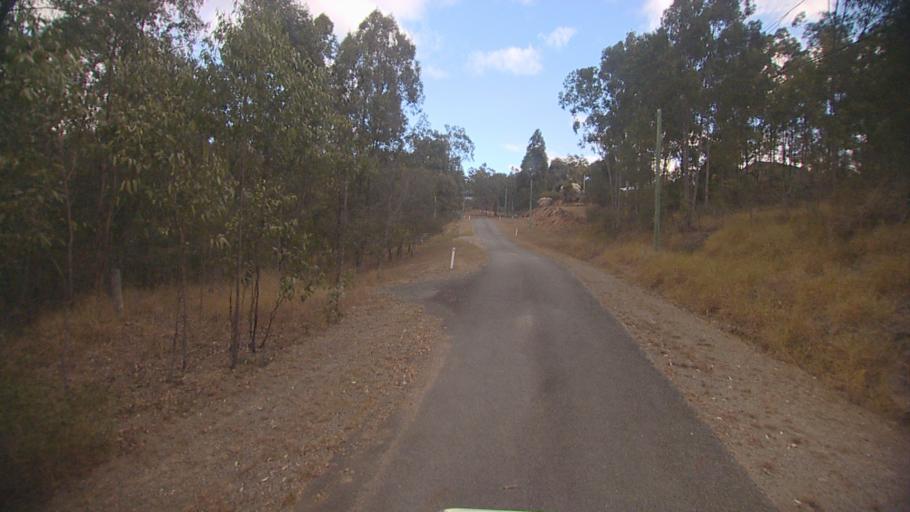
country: AU
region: Queensland
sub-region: Logan
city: Cedar Vale
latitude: -27.9336
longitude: 153.0558
